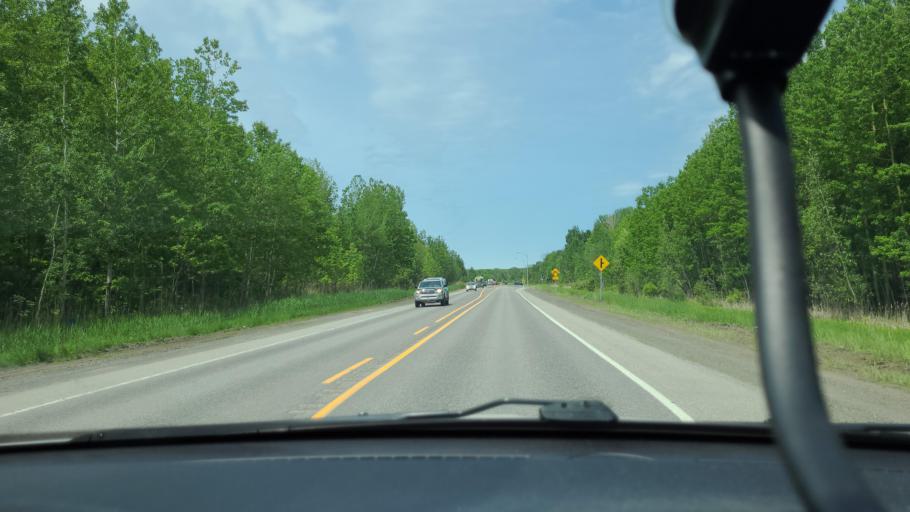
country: CA
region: Quebec
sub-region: Lanaudiere
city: Saint-Jacques
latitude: 45.9696
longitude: -73.5332
